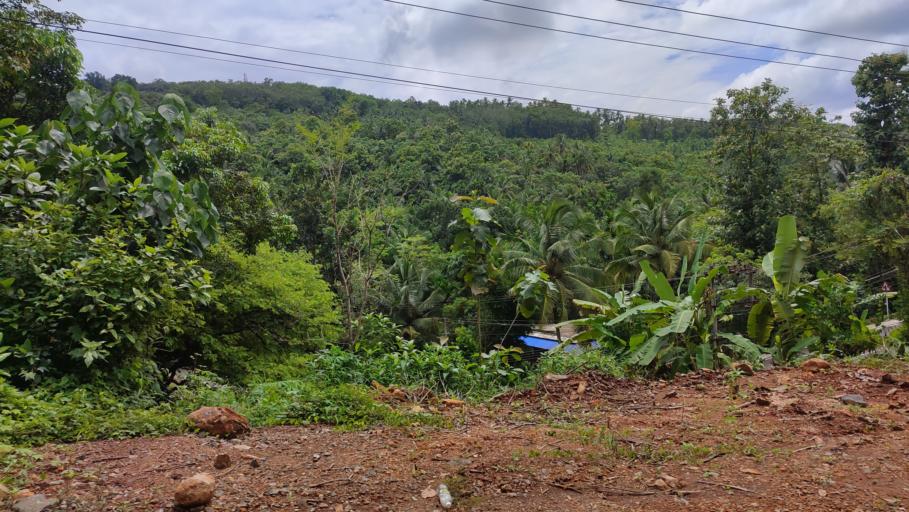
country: IN
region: Kerala
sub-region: Kasaragod District
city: Nileshwar
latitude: 12.2878
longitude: 75.2676
